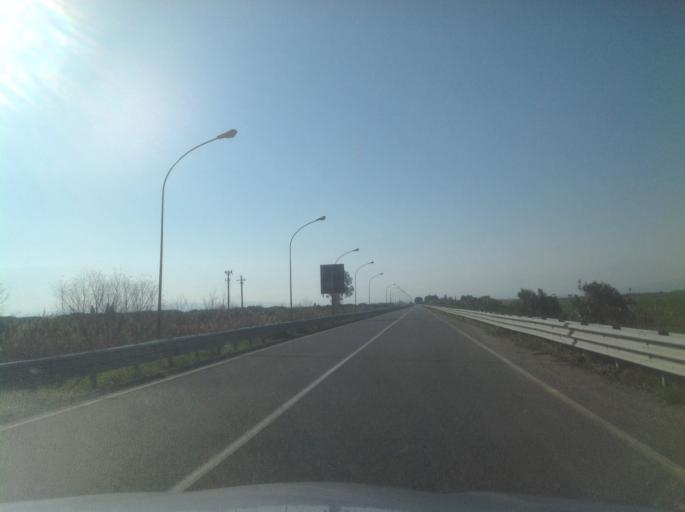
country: IT
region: Calabria
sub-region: Provincia di Cosenza
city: Sibari
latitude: 39.7273
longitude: 16.4940
